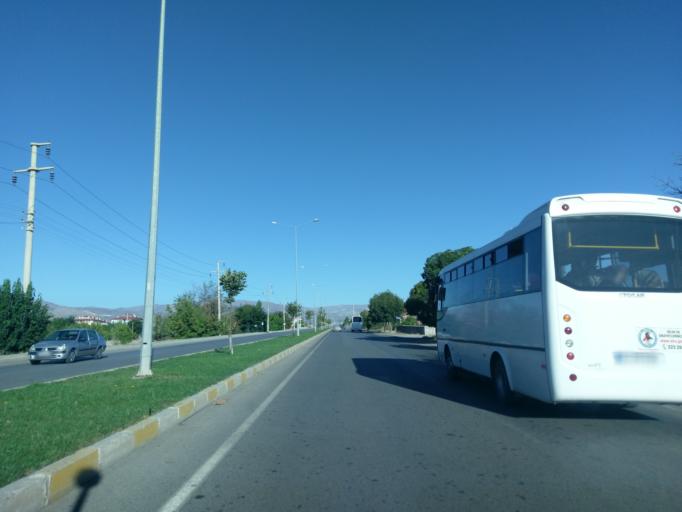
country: TR
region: Erzincan
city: Erzincan
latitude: 39.7542
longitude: 39.4525
